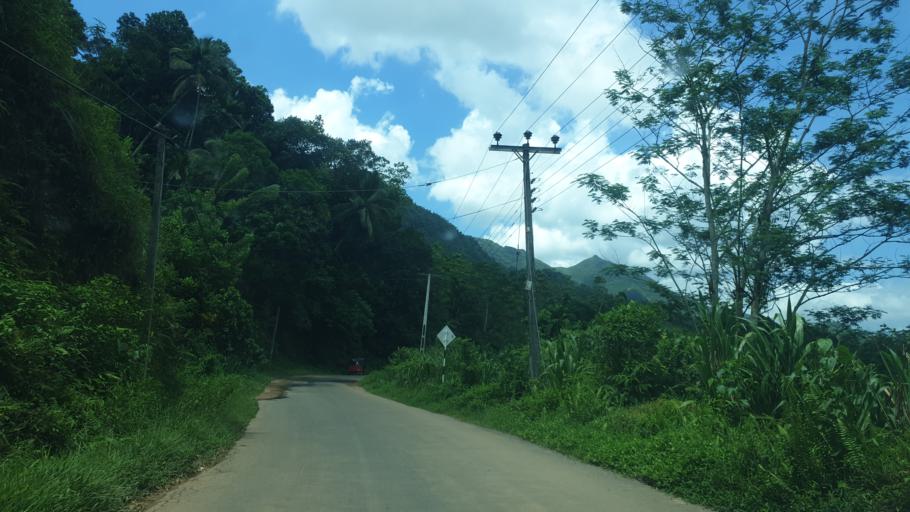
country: LK
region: Sabaragamuwa
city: Ratnapura
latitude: 6.4817
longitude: 80.4110
